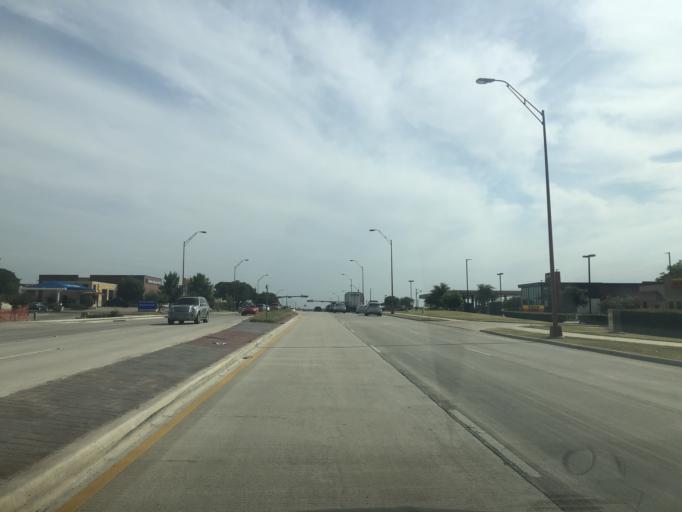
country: US
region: Texas
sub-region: Tarrant County
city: Benbrook
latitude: 32.6718
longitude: -97.4708
